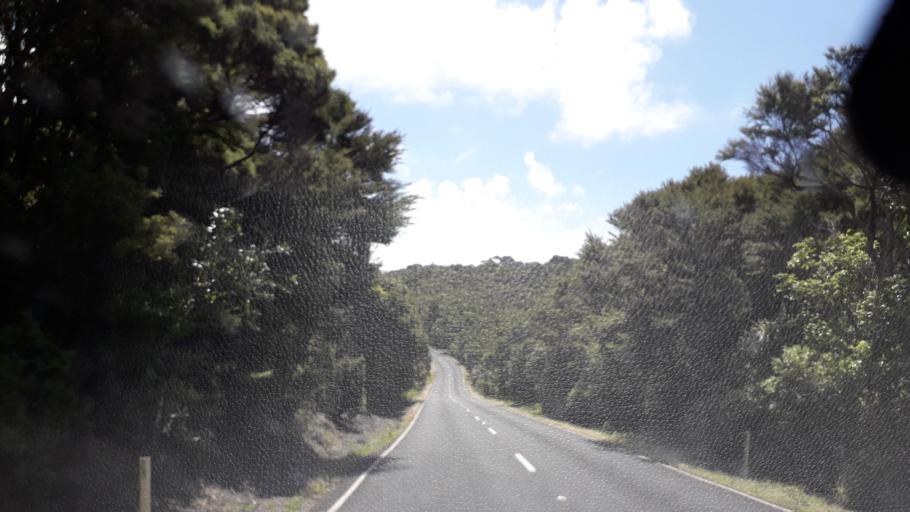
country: NZ
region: Northland
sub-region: Far North District
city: Paihia
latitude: -35.2491
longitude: 174.2593
